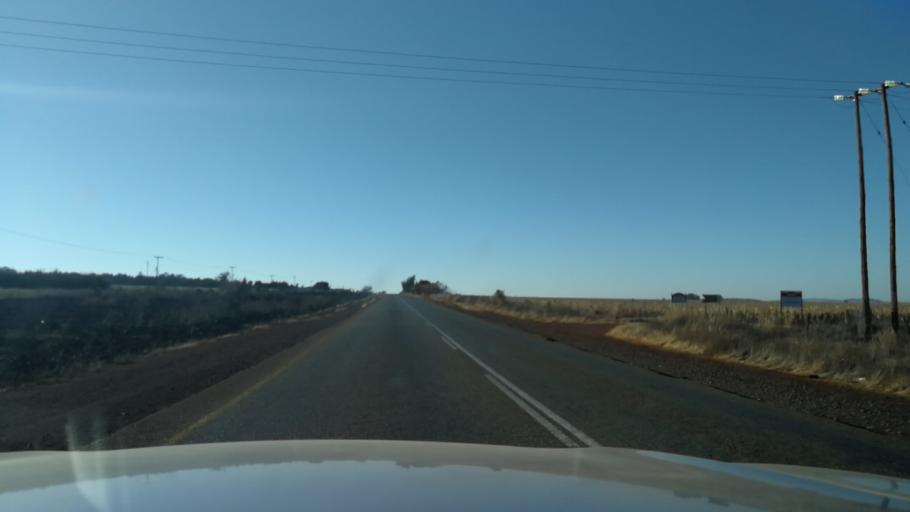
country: ZA
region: North-West
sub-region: Bojanala Platinum District Municipality
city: Koster
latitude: -25.9323
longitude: 27.1377
